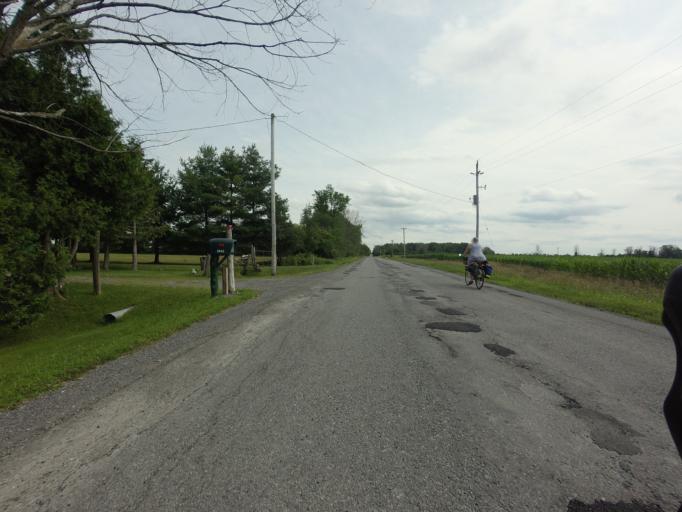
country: CA
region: Ontario
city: Bells Corners
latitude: 45.1115
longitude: -75.5977
